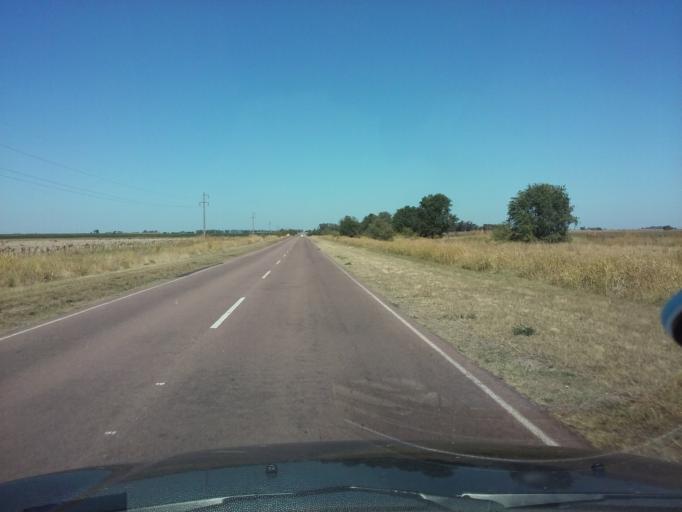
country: AR
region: La Pampa
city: Colonia Baron
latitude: -36.2557
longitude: -63.9428
